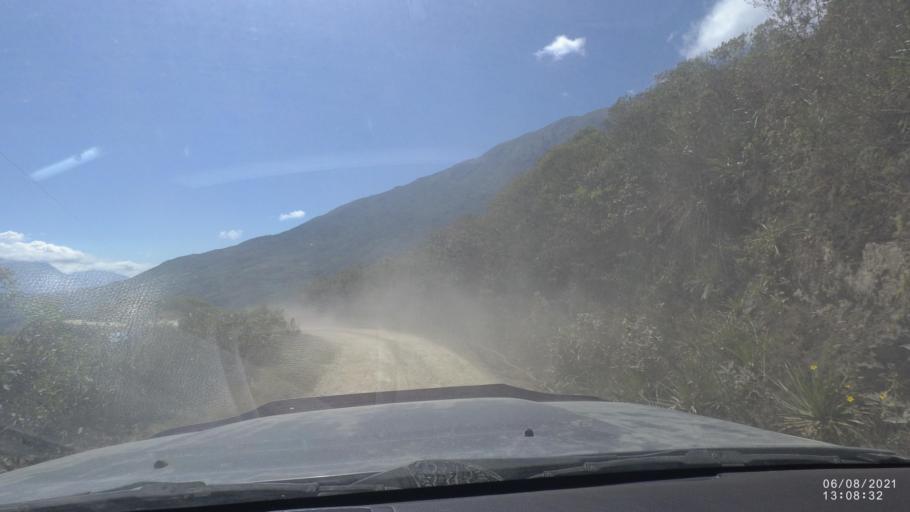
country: BO
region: La Paz
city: Quime
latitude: -16.7277
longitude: -66.7069
